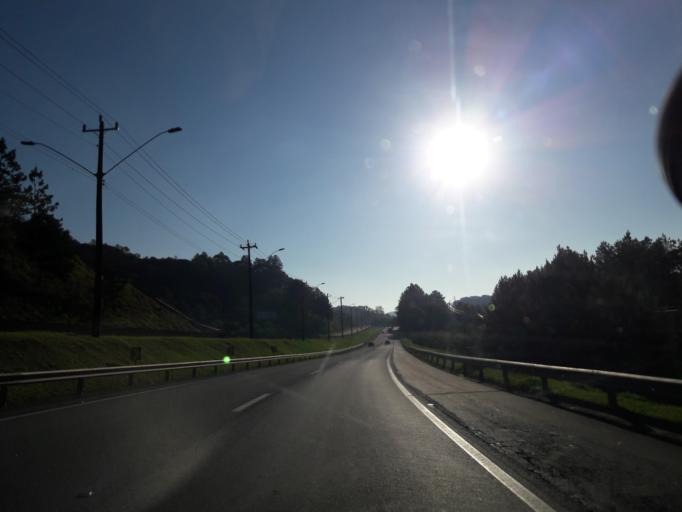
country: BR
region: Sao Paulo
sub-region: Juquitiba
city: Juquitiba
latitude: -23.9310
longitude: -47.0006
